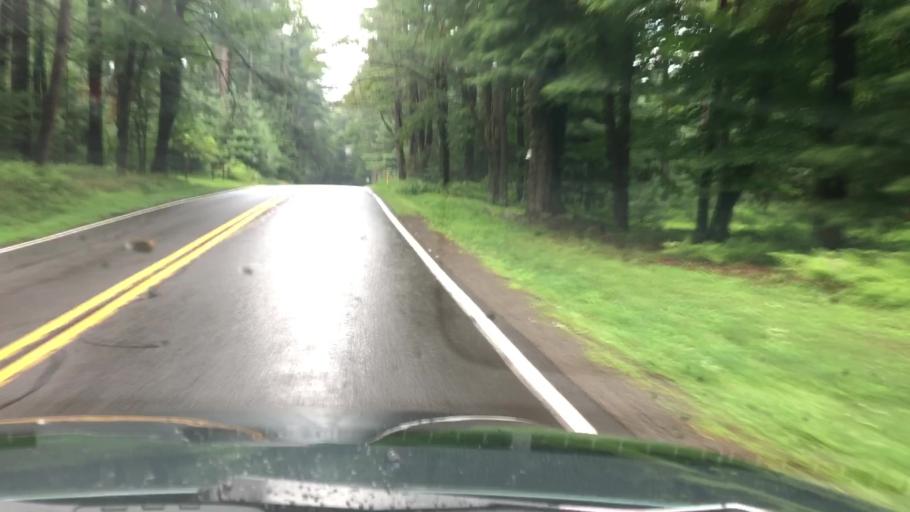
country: US
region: Pennsylvania
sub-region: Monroe County
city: Mountainhome
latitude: 41.3197
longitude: -75.2098
